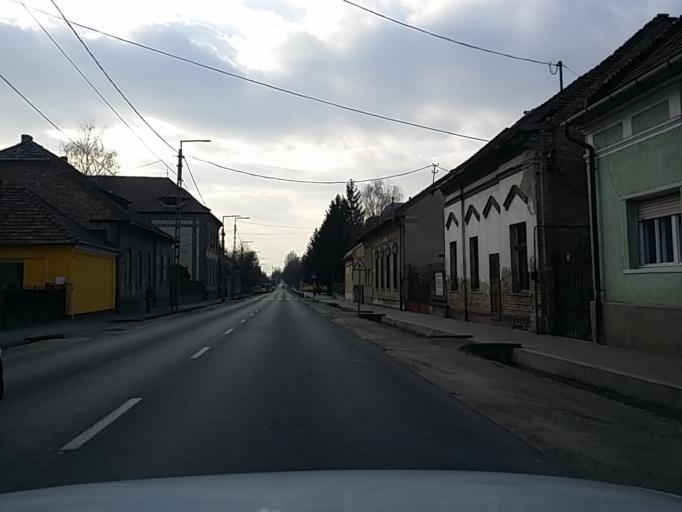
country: HU
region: Borsod-Abauj-Zemplen
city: Putnok
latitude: 48.2956
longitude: 20.4295
